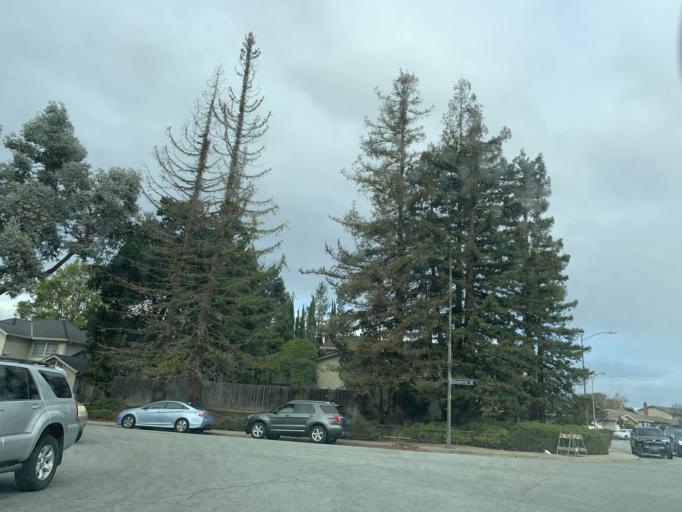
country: US
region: California
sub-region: Santa Clara County
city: Monte Sereno
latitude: 37.2691
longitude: -121.9876
